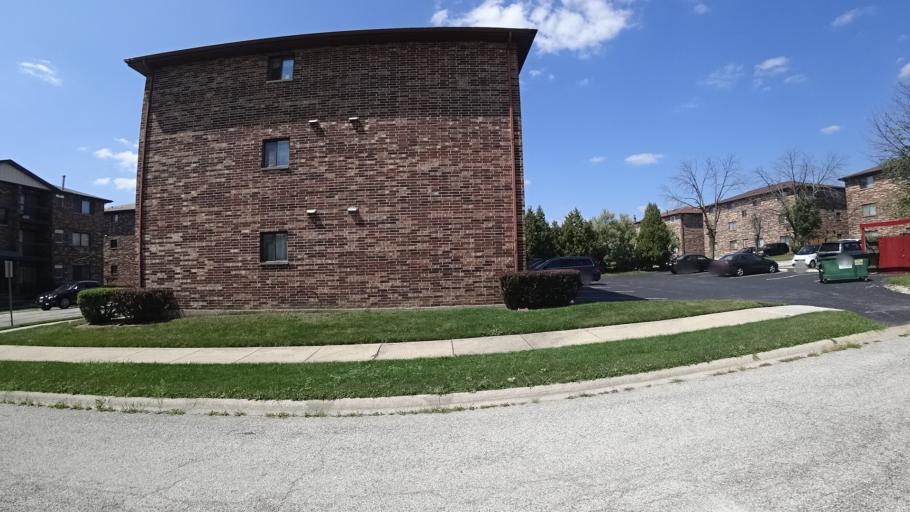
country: US
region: Illinois
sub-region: Cook County
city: Orland Park
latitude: 41.6203
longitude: -87.8391
